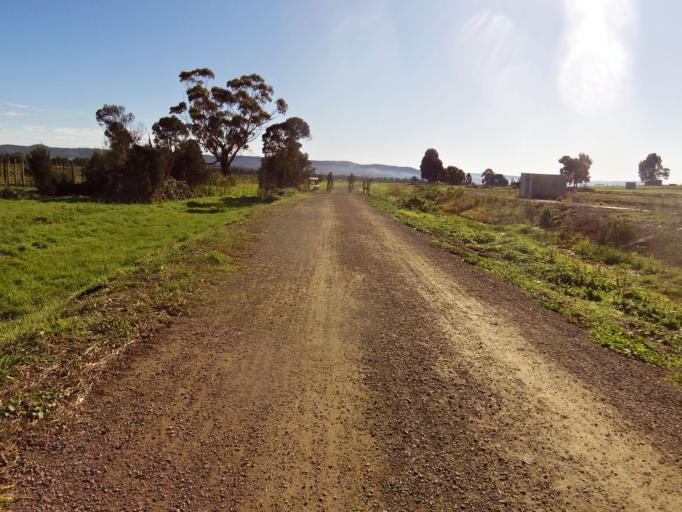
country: AU
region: Victoria
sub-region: Yarra Ranges
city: Lilydale
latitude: -37.7175
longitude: 145.3677
